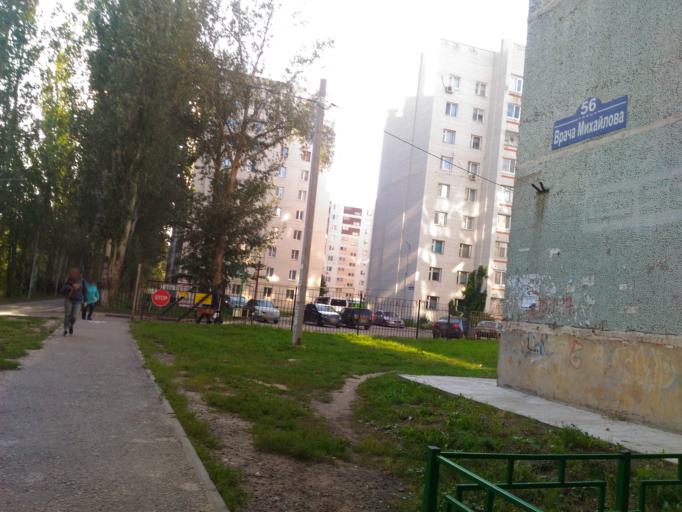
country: RU
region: Ulyanovsk
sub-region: Ulyanovskiy Rayon
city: Ulyanovsk
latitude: 54.3530
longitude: 48.5295
